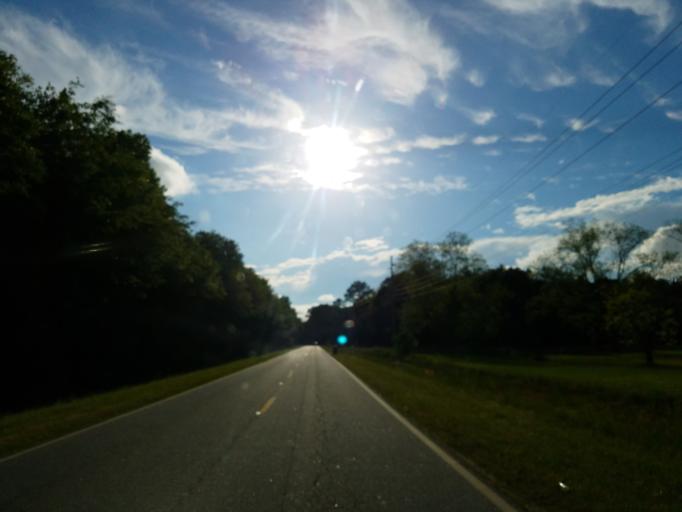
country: US
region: Georgia
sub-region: Crisp County
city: Cordele
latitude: 32.0044
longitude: -83.7905
